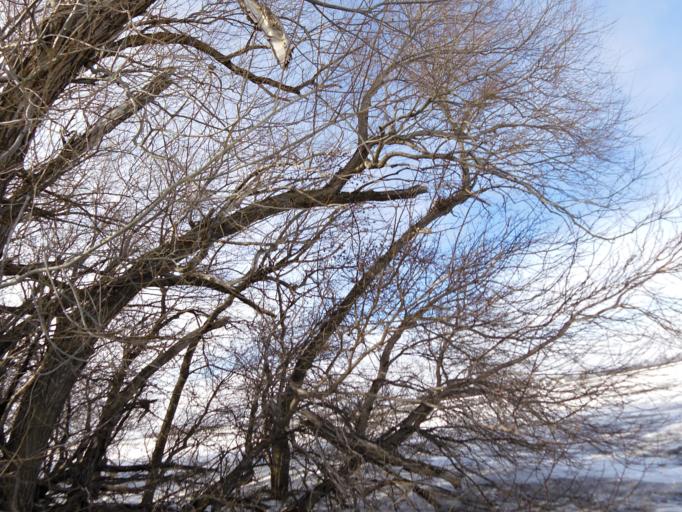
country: US
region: North Dakota
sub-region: Walsh County
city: Grafton
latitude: 48.3993
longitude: -97.2086
